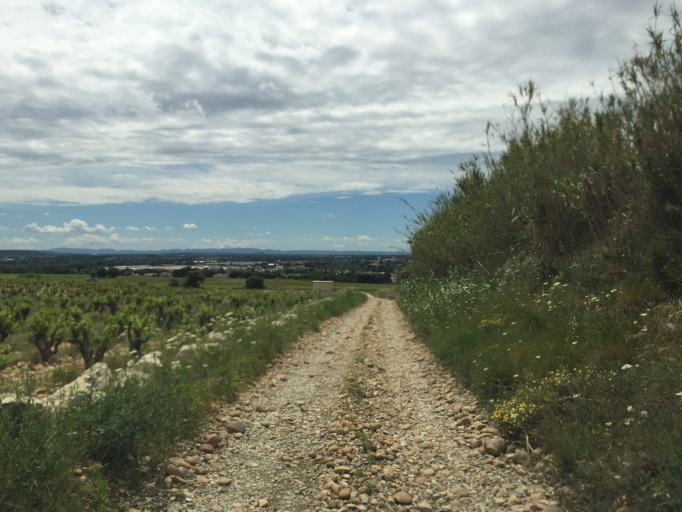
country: FR
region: Provence-Alpes-Cote d'Azur
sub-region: Departement du Vaucluse
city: Bedarrides
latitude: 44.0417
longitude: 4.8713
